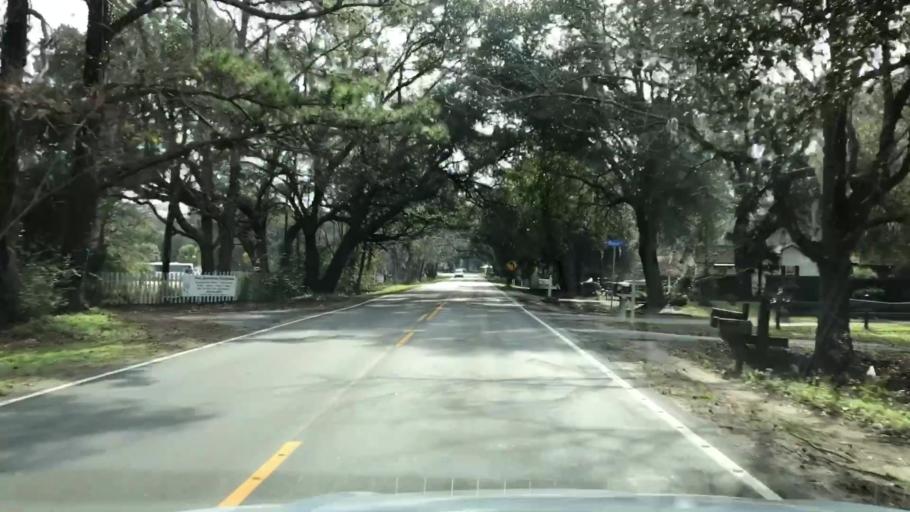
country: US
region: South Carolina
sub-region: Charleston County
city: Shell Point
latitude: 32.7347
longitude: -80.0316
